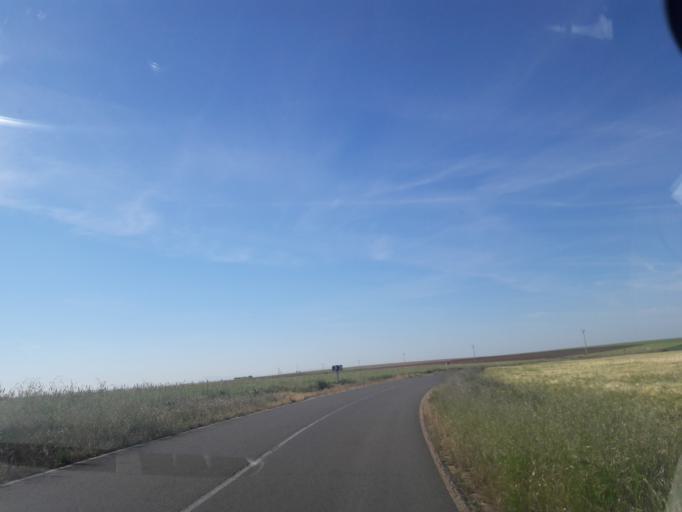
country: ES
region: Castille and Leon
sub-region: Provincia de Salamanca
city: Tardaguila
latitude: 41.1107
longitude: -5.5730
